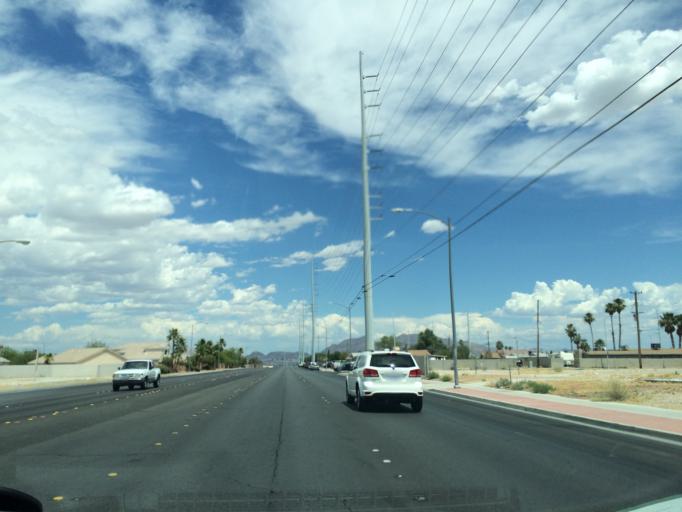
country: US
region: Nevada
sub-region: Clark County
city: Las Vegas
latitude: 36.2030
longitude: -115.1576
